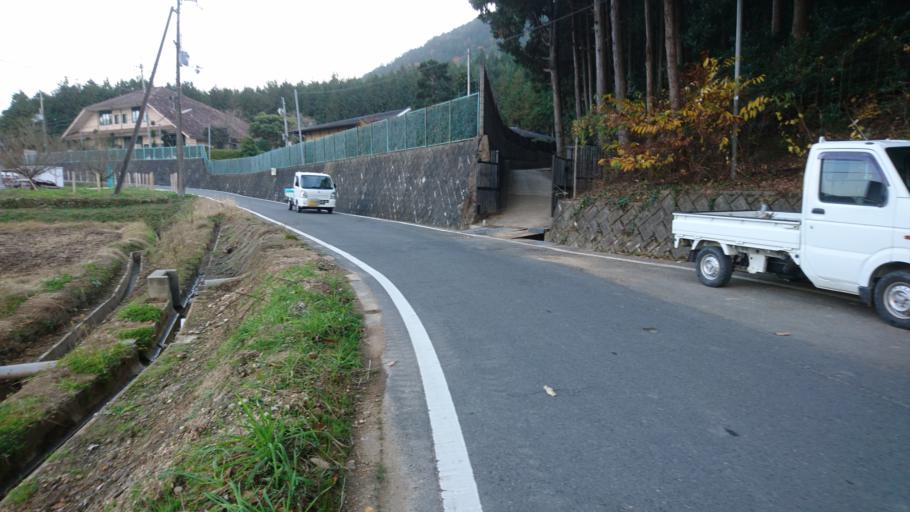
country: JP
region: Kyoto
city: Kameoka
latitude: 35.0463
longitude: 135.4717
